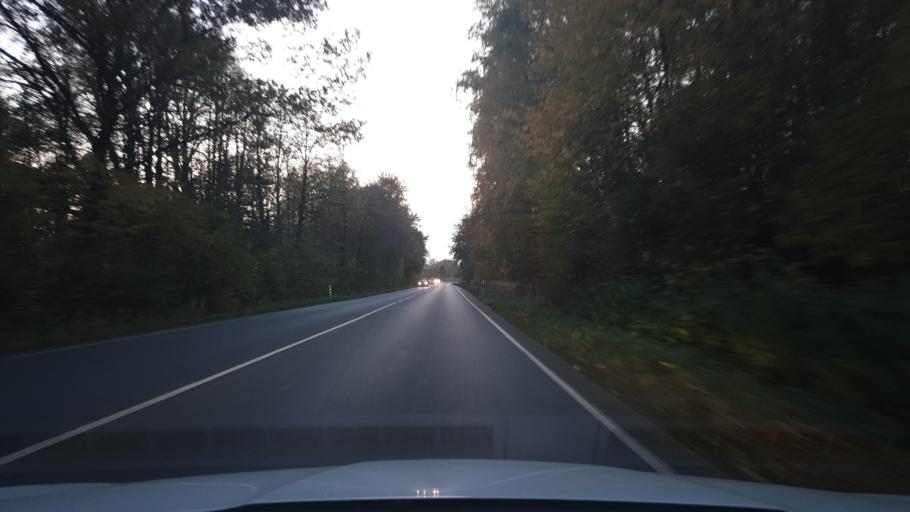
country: DE
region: North Rhine-Westphalia
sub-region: Regierungsbezirk Detmold
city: Herford
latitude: 52.0997
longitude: 8.6250
